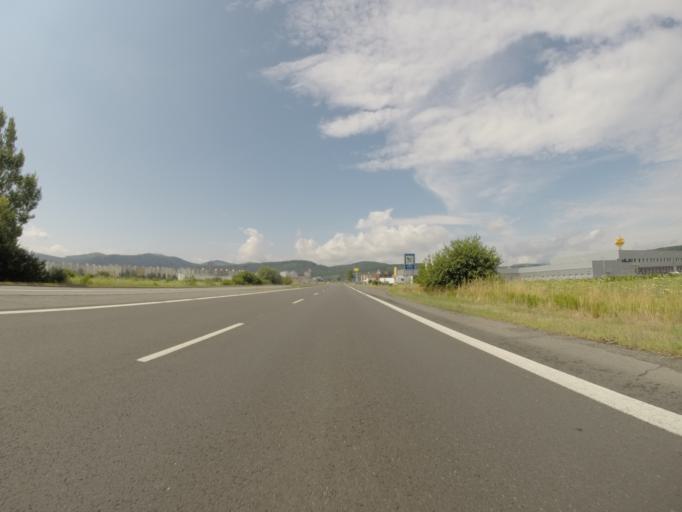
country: SK
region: Banskobystricky
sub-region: Okres Banska Bystrica
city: Zvolen
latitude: 48.5884
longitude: 19.1092
